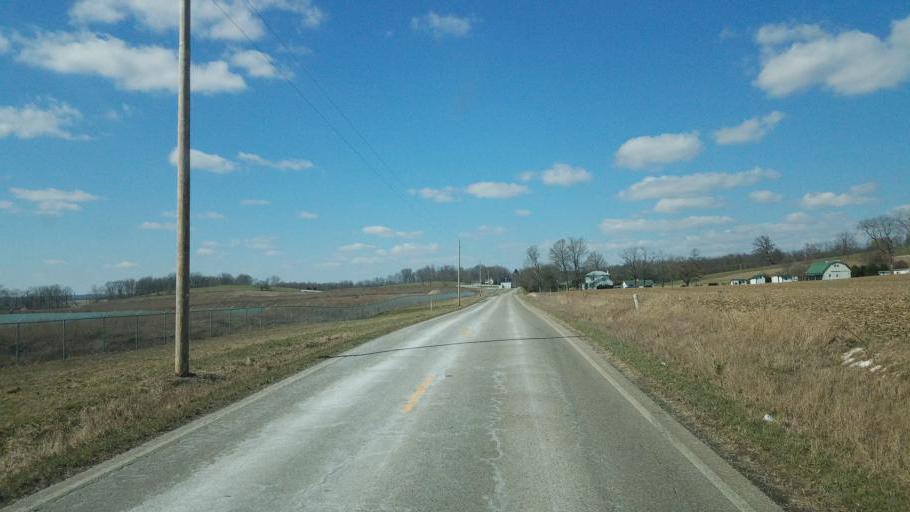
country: US
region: Ohio
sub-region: Knox County
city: Fredericktown
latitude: 40.4534
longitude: -82.5158
